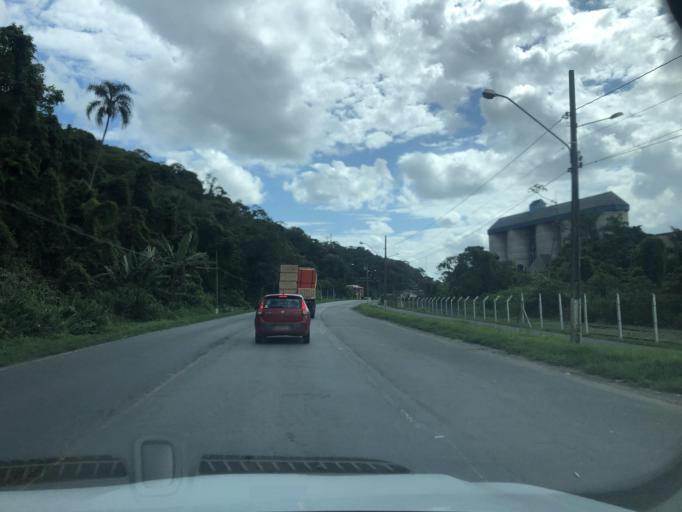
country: BR
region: Santa Catarina
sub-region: Sao Francisco Do Sul
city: Sao Francisco do Sul
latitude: -26.2385
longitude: -48.6305
